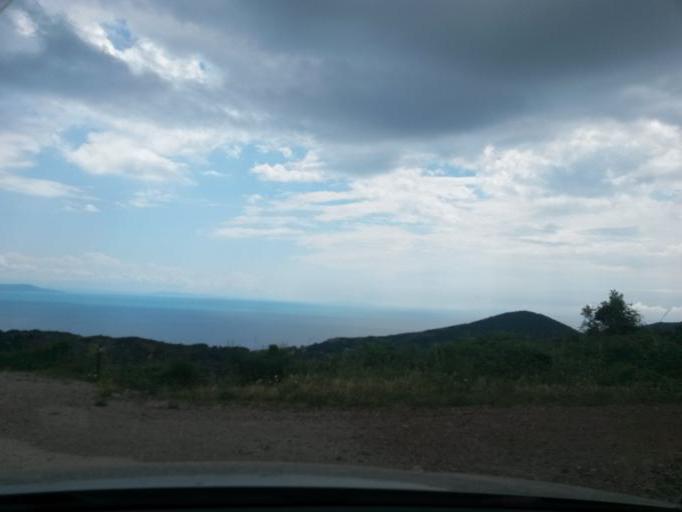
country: IT
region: Tuscany
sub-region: Provincia di Livorno
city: Rio nell'Elba
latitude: 42.8234
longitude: 10.4029
